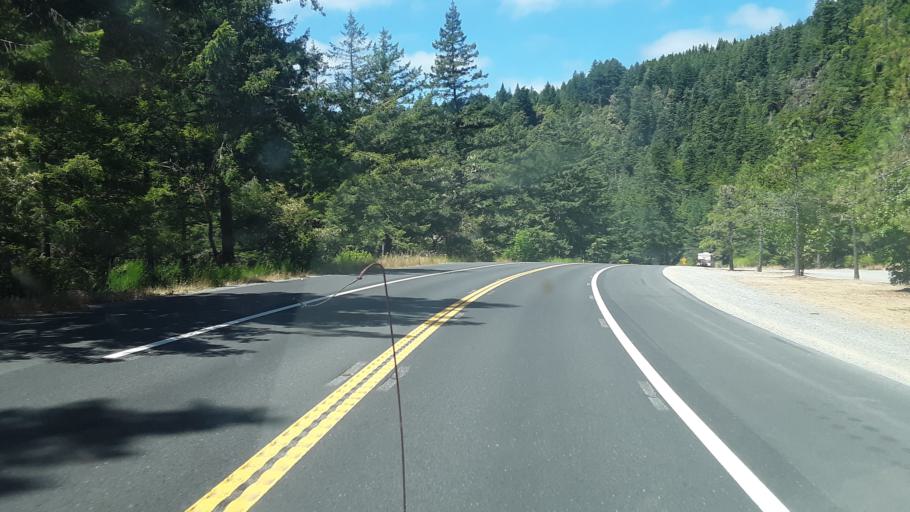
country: US
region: California
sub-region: Del Norte County
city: Bertsch-Oceanview
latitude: 41.8093
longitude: -124.0466
